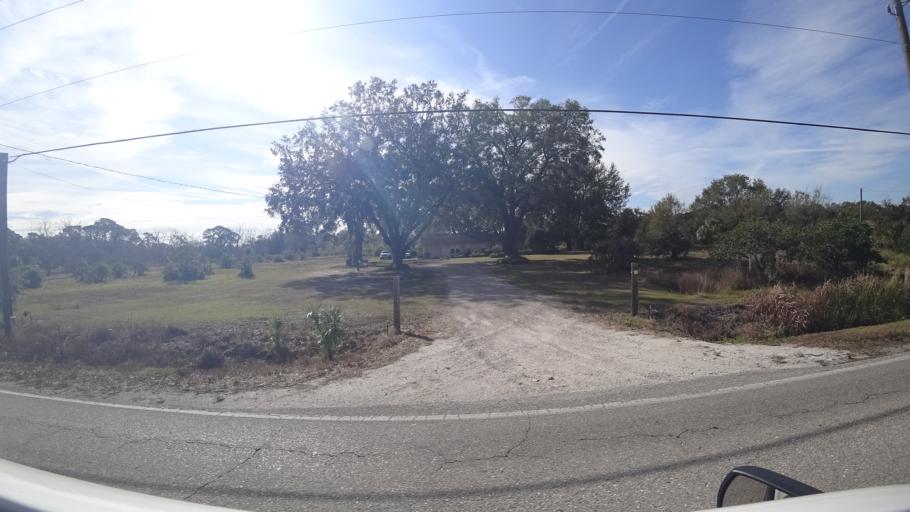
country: US
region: Florida
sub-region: Manatee County
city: Memphis
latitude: 27.6014
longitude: -82.5254
